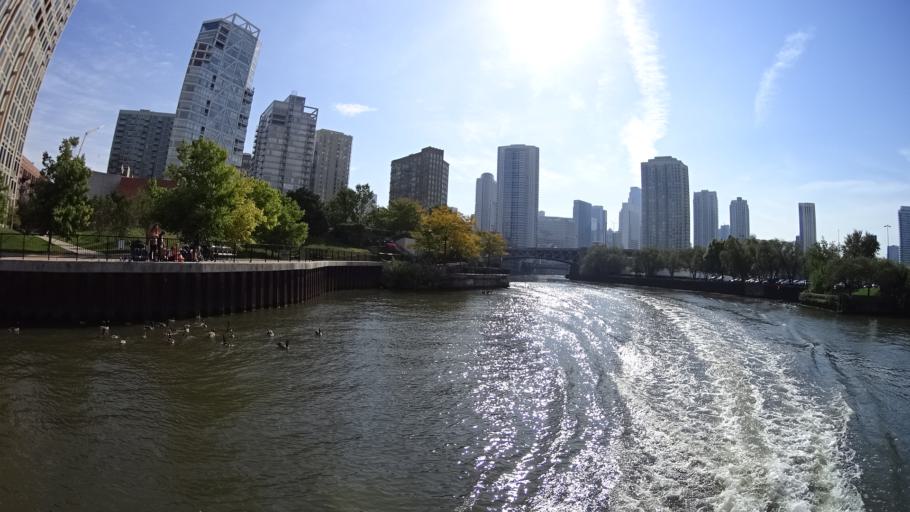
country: US
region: Illinois
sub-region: Cook County
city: Chicago
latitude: 41.8942
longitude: -87.6440
